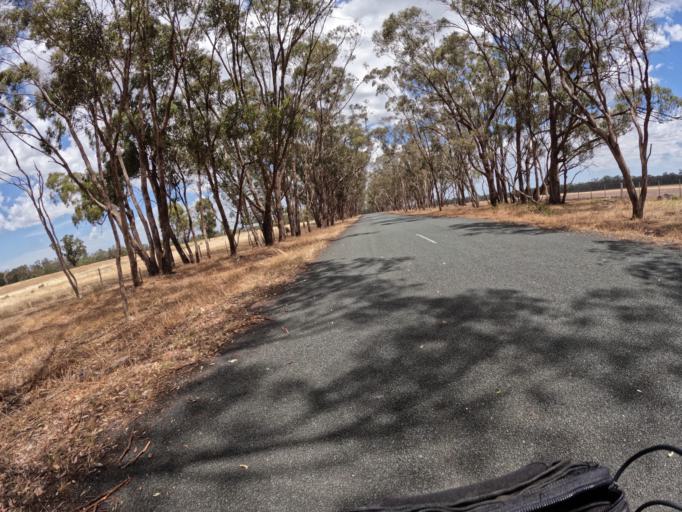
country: AU
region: Victoria
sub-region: Greater Shepparton
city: Shepparton
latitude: -36.6801
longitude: 145.1944
